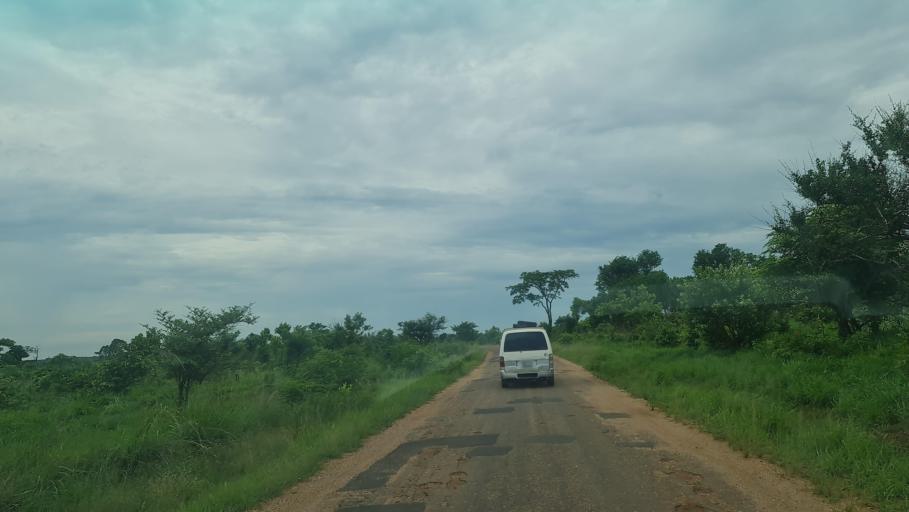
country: MW
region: Southern Region
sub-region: Nsanje District
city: Nsanje
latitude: -17.6833
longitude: 35.7263
